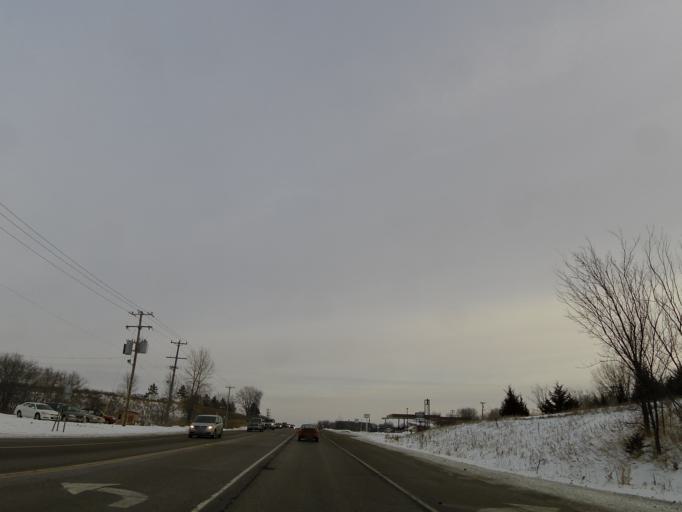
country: US
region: Minnesota
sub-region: Hennepin County
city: Saint Bonifacius
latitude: 44.9007
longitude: -93.7335
